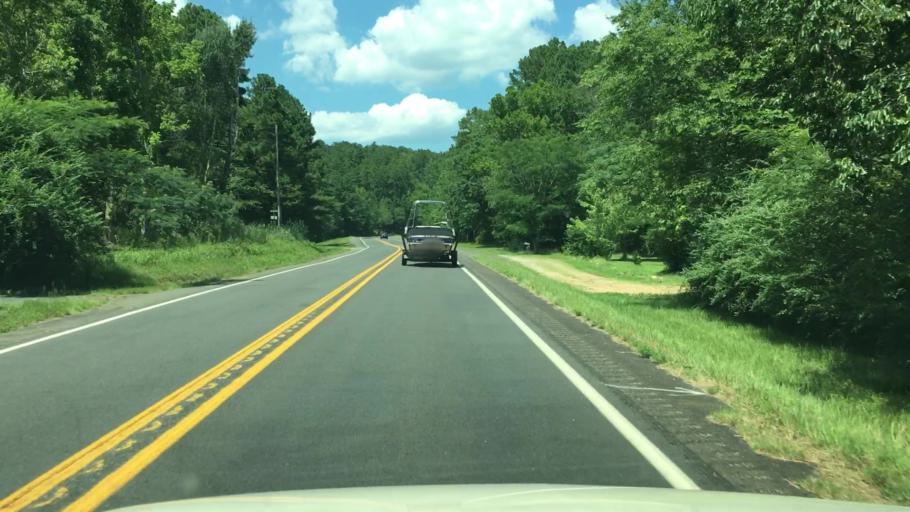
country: US
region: Arkansas
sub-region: Garland County
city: Lake Hamilton
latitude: 34.3493
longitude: -93.1842
